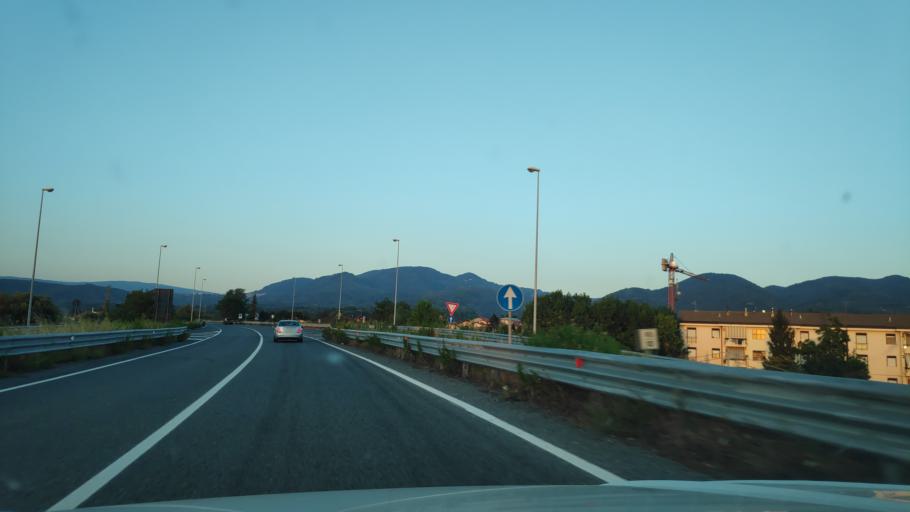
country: IT
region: Calabria
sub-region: Provincia di Reggio Calabria
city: Cinque Frondi
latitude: 38.4178
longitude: 16.0838
